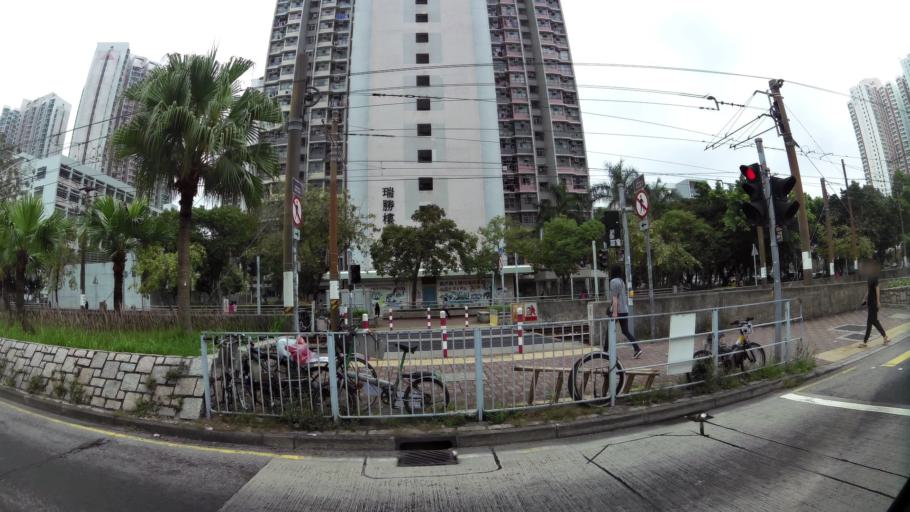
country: HK
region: Yuen Long
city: Yuen Long Kau Hui
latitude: 22.4585
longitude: 113.9981
